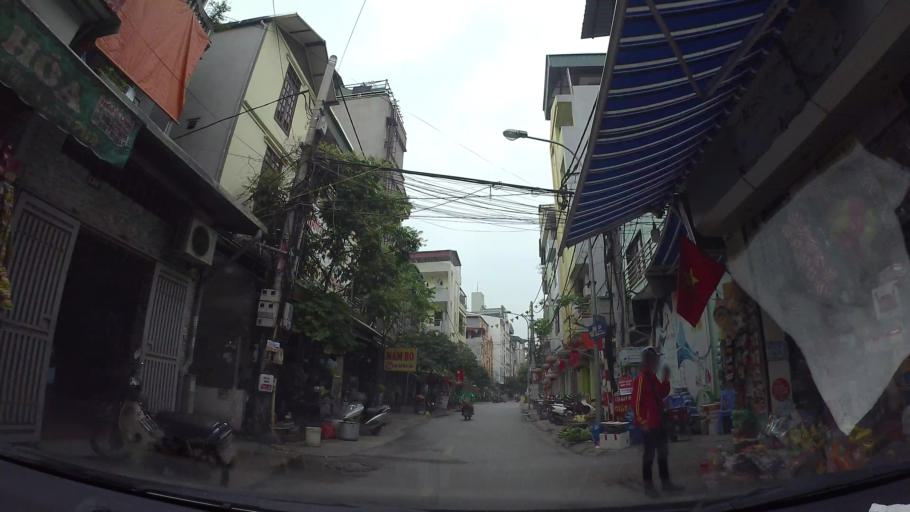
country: VN
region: Ha Noi
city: Hai BaTrung
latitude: 20.9908
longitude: 105.8591
